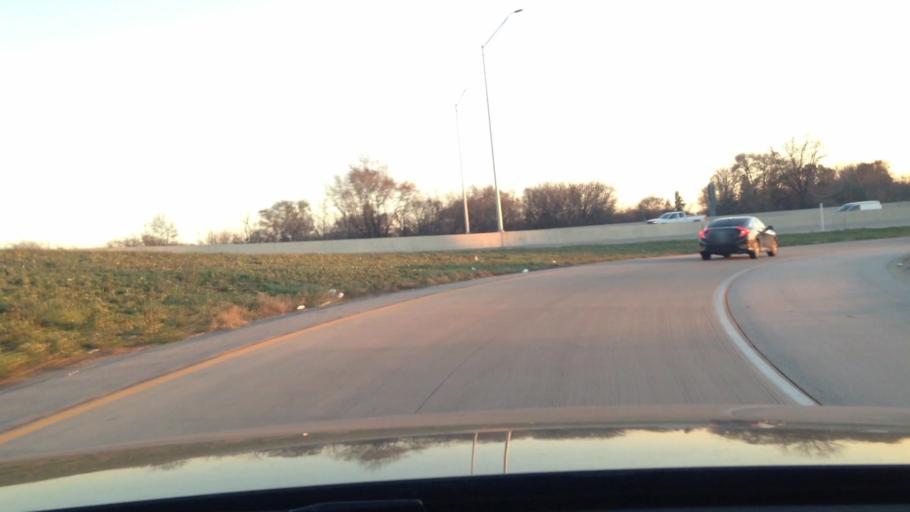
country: US
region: Illinois
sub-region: Kane County
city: East Dundee
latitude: 42.0657
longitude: -88.2589
